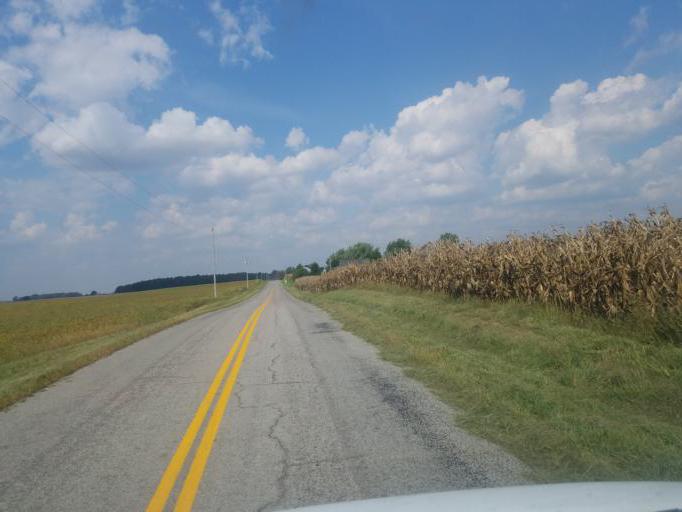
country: US
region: Ohio
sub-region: Hardin County
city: Ada
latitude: 40.6385
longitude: -83.8836
